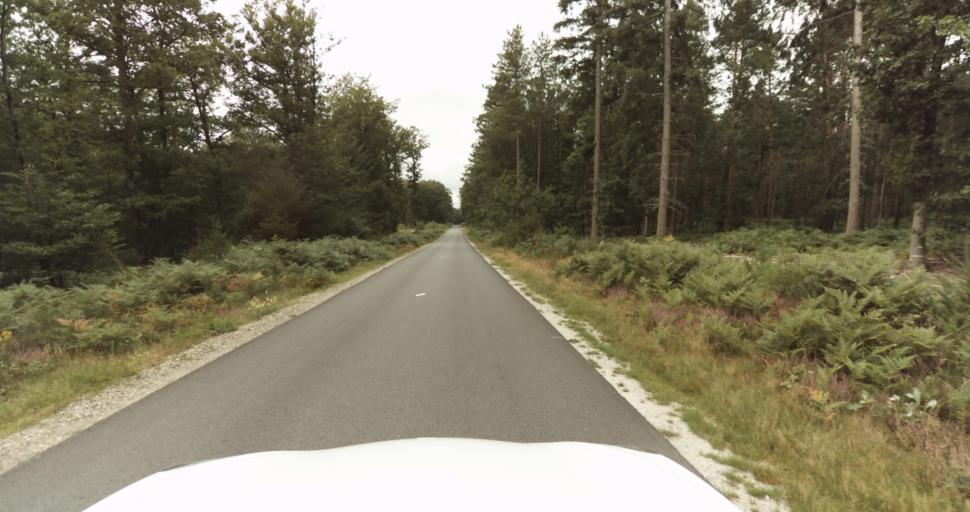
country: FR
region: Haute-Normandie
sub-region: Departement de l'Eure
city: Saint-Sebastien-de-Morsent
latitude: 48.9633
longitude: 1.0536
